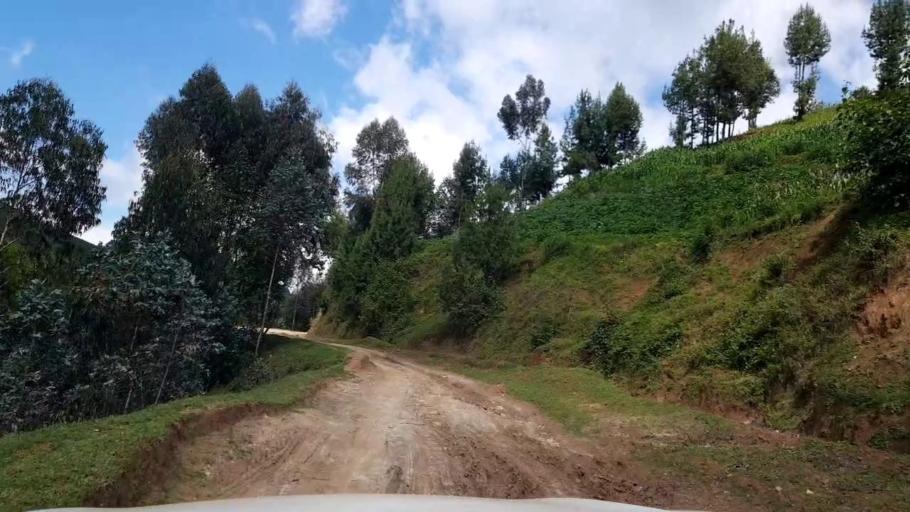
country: RW
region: Western Province
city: Kibuye
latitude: -1.8816
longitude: 29.4689
